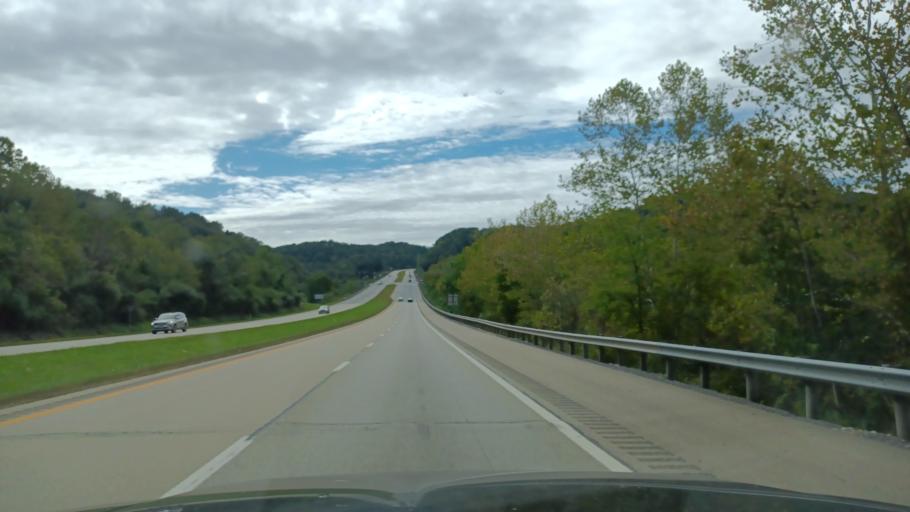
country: US
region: West Virginia
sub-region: Doddridge County
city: West Union
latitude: 39.2918
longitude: -80.7649
